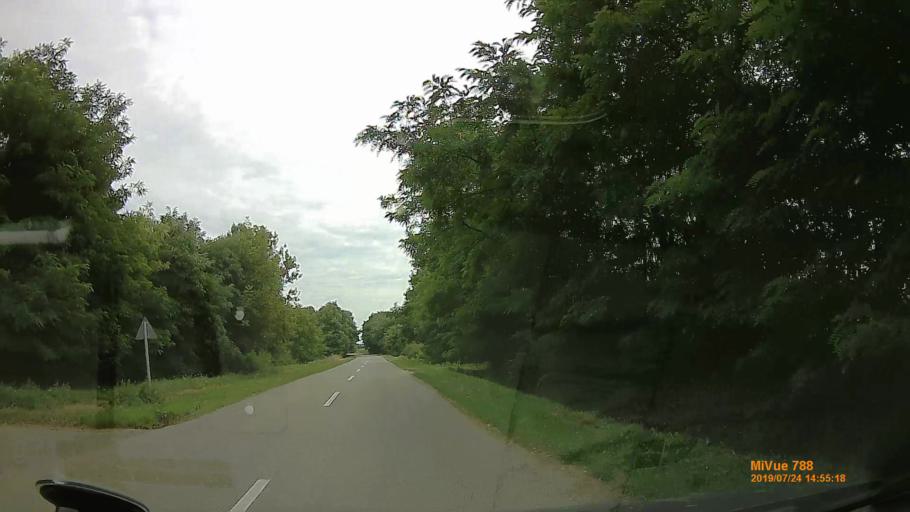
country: HU
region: Szabolcs-Szatmar-Bereg
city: Aranyosapati
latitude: 48.2571
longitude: 22.3146
